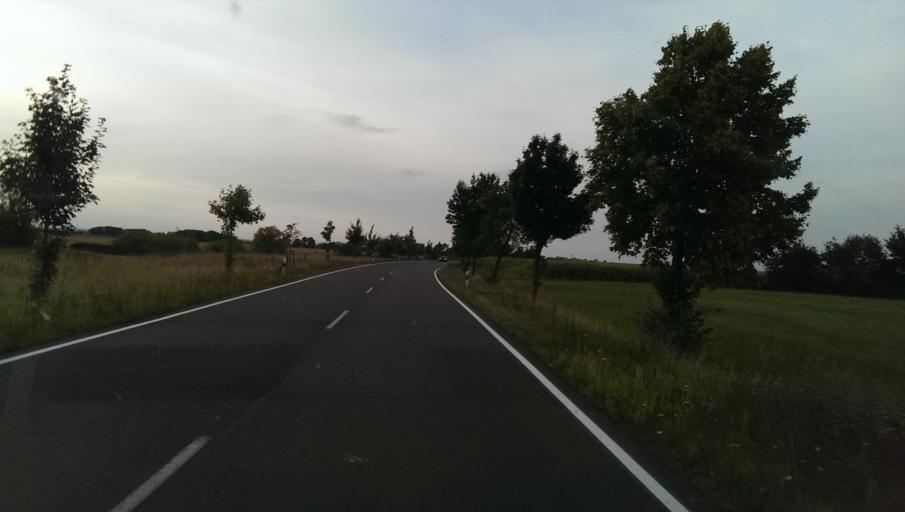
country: DE
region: Saxony-Anhalt
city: Kemberg
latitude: 51.7957
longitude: 12.6515
